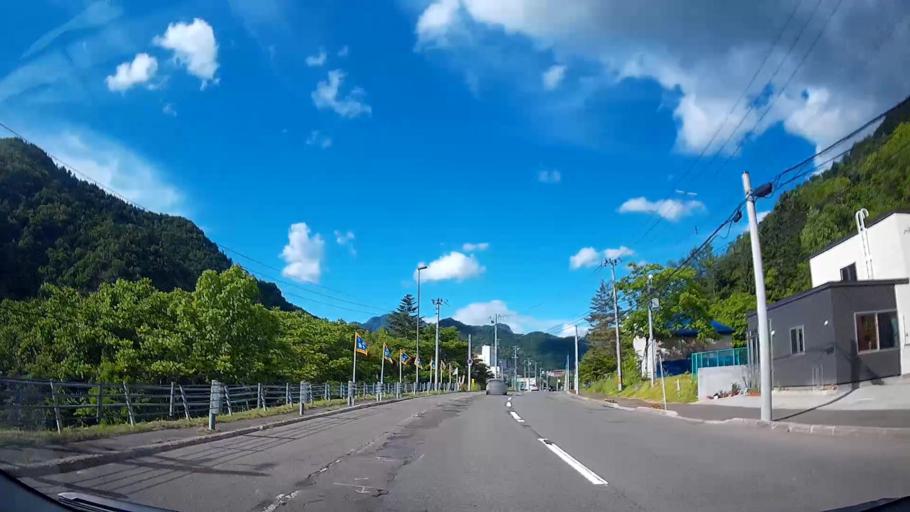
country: JP
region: Hokkaido
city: Sapporo
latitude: 42.9599
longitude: 141.1569
